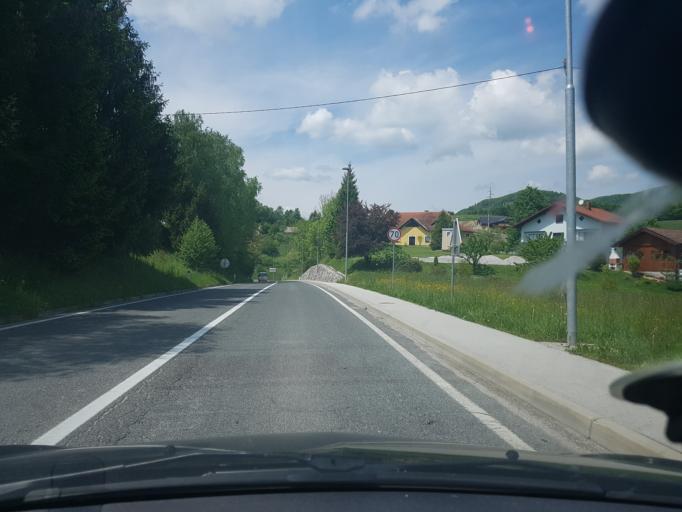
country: SI
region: Rogaska Slatina
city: Rogaska Slatina
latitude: 46.2483
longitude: 15.6456
